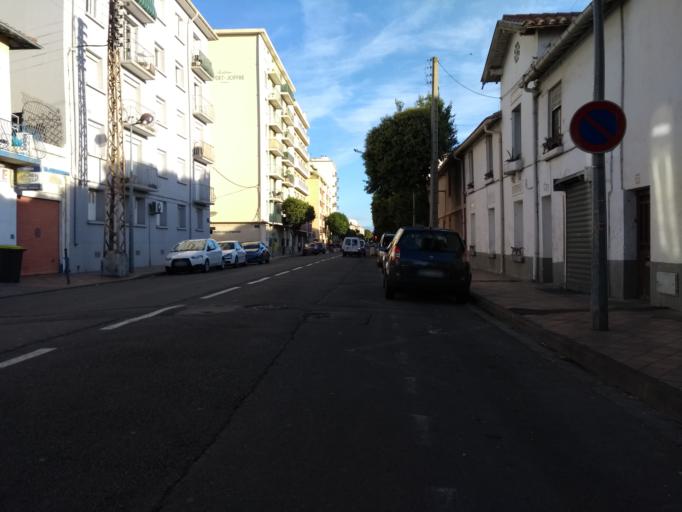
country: FR
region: Languedoc-Roussillon
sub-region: Departement des Pyrenees-Orientales
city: Perpignan
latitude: 42.7078
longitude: 2.8914
